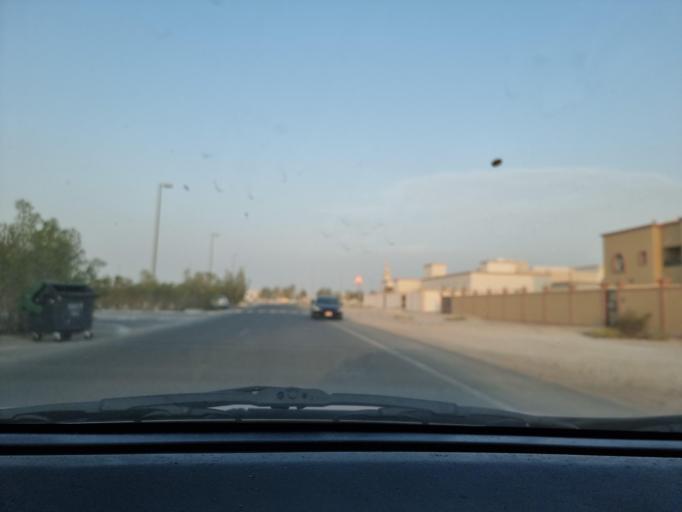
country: AE
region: Abu Dhabi
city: Abu Dhabi
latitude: 24.3815
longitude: 54.7037
